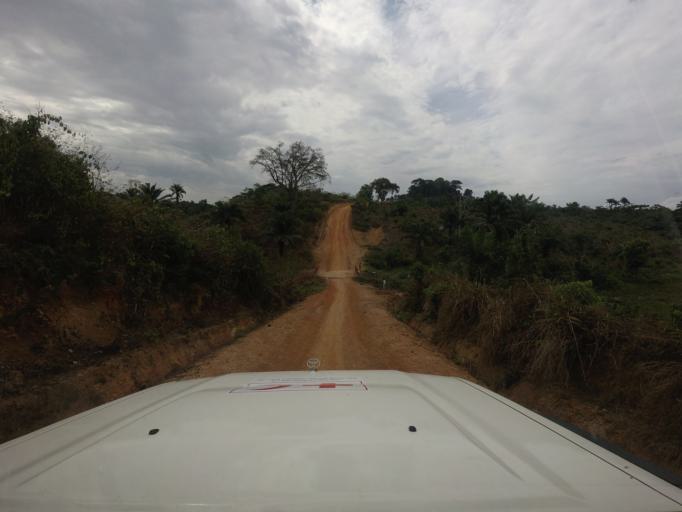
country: SL
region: Eastern Province
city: Buedu
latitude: 8.2524
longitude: -10.2282
